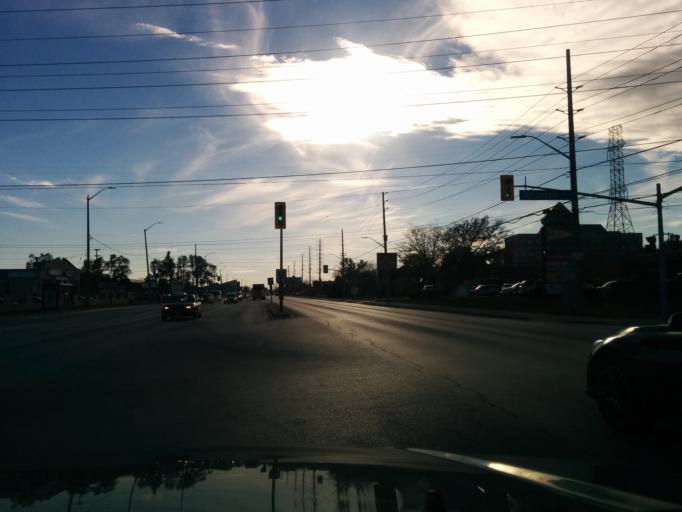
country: CA
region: Ontario
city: Etobicoke
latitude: 43.6191
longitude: -79.5734
